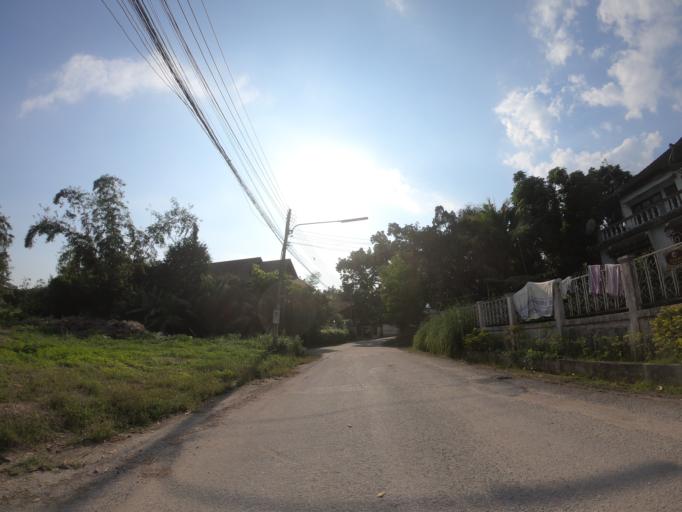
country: TH
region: Chiang Mai
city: San Sai
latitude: 18.8317
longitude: 99.0059
